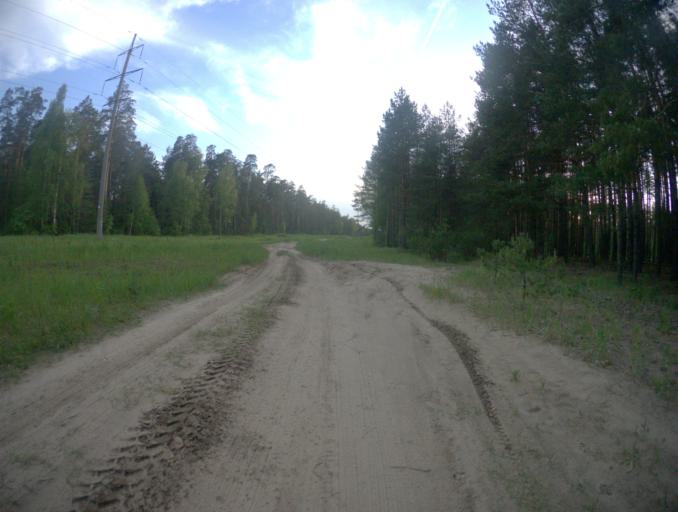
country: RU
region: Vladimir
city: Gus'-Khrustal'nyy
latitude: 55.6330
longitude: 40.6862
